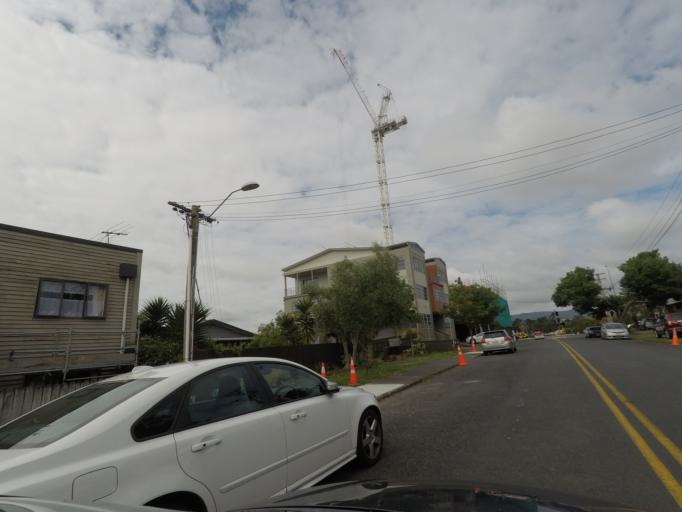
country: NZ
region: Auckland
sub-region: Auckland
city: Rosebank
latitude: -36.8745
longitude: 174.6285
